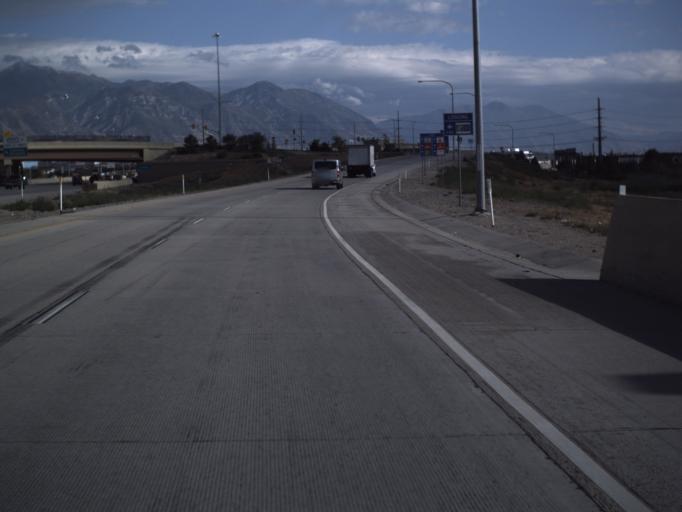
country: US
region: Utah
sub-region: Utah County
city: American Fork
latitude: 40.3621
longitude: -111.7886
